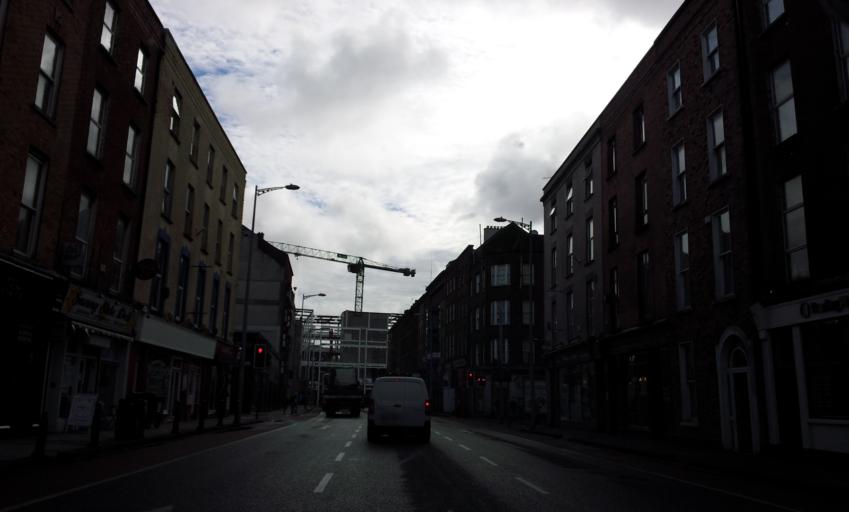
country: IE
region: Munster
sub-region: County Cork
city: Cork
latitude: 51.8976
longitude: -8.4780
